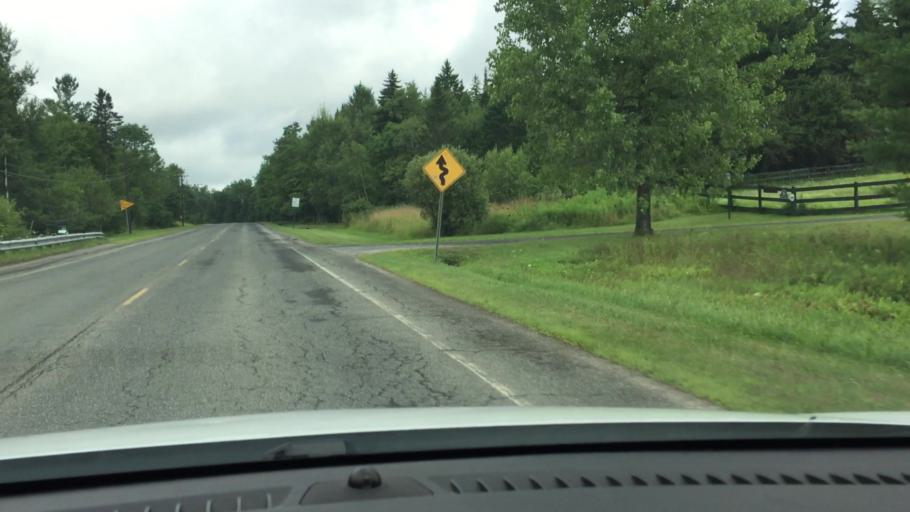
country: US
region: Massachusetts
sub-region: Berkshire County
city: Hinsdale
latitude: 42.4434
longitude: -73.0532
